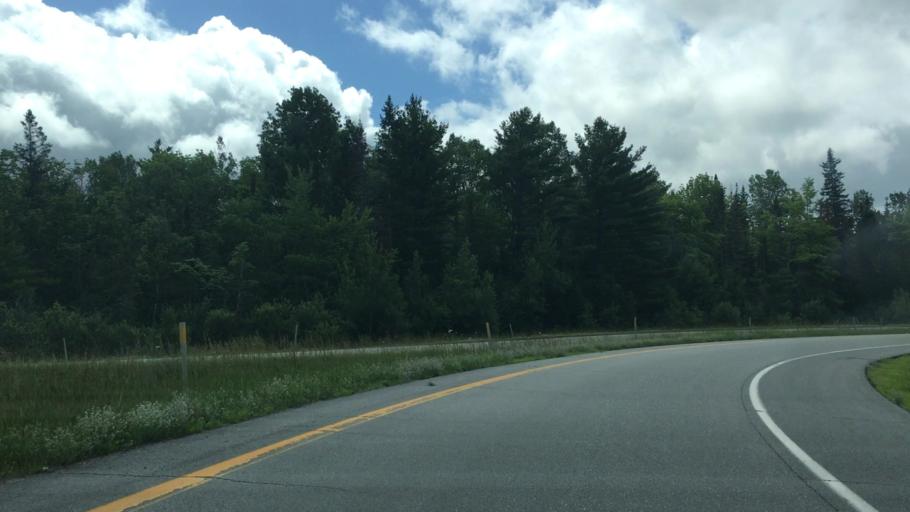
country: US
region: Maine
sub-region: Penobscot County
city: Etna
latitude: 44.7830
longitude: -69.1011
